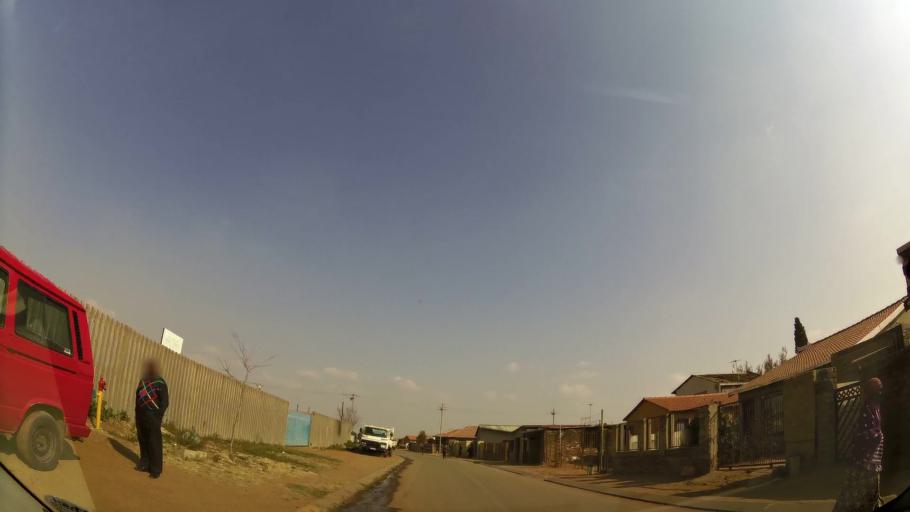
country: ZA
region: Gauteng
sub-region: Ekurhuleni Metropolitan Municipality
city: Springs
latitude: -26.1063
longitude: 28.4790
